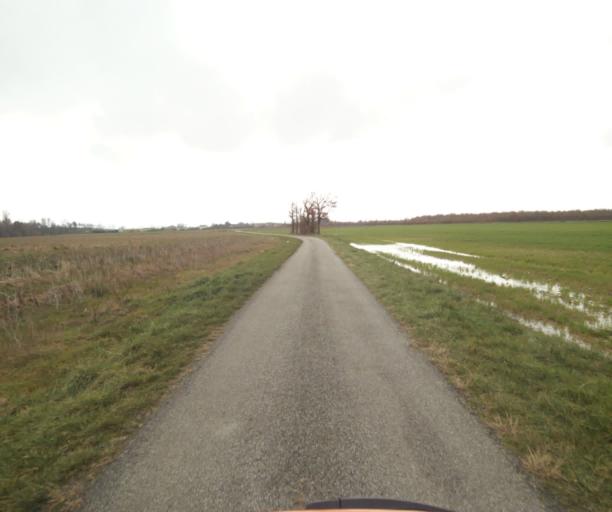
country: FR
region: Languedoc-Roussillon
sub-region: Departement de l'Aude
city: Belpech
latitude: 43.1757
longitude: 1.6922
